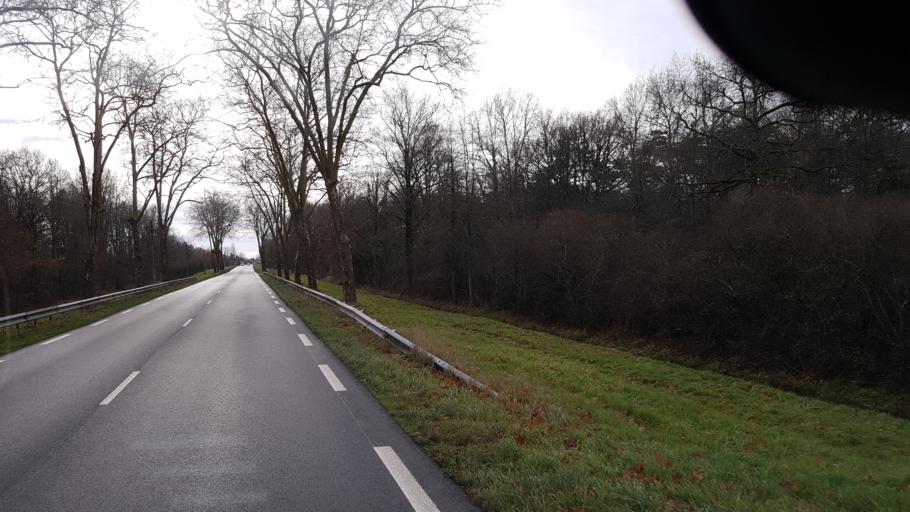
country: FR
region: Centre
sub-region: Departement du Loiret
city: La Ferte-Saint-Aubin
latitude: 47.7781
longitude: 1.9359
